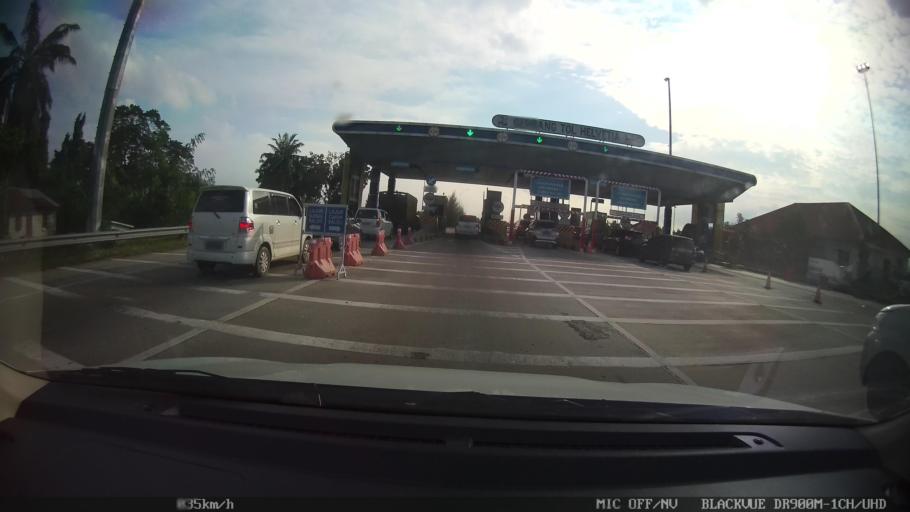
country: ID
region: North Sumatra
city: Sunggal
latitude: 3.6304
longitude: 98.6331
